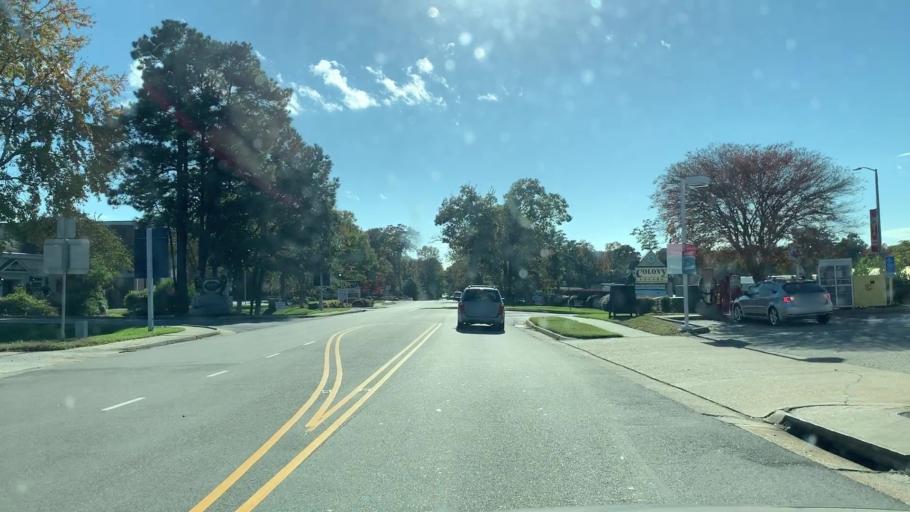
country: US
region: Virginia
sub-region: James City County
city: Williamsburg
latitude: 37.2532
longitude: -76.7327
